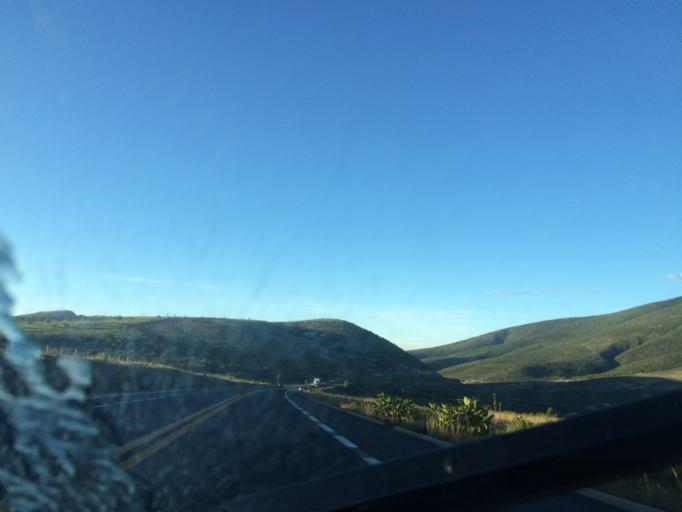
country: MX
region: Puebla
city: Morelos Canada
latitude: 18.6879
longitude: -97.4609
